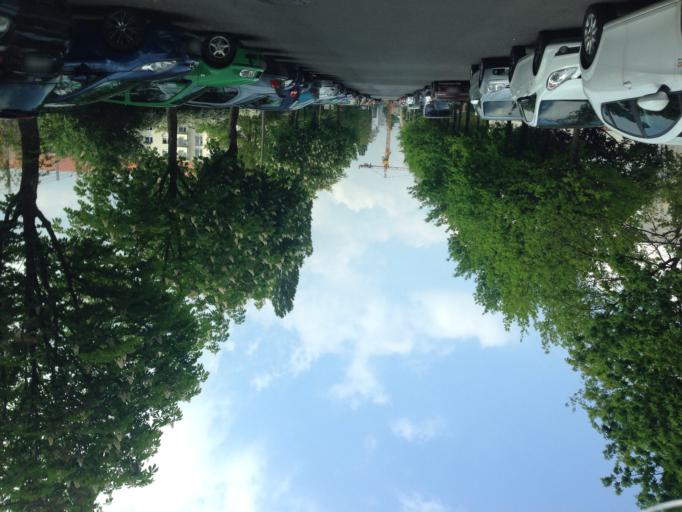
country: DE
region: Saxony
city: Dresden
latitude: 51.0477
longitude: 13.7580
